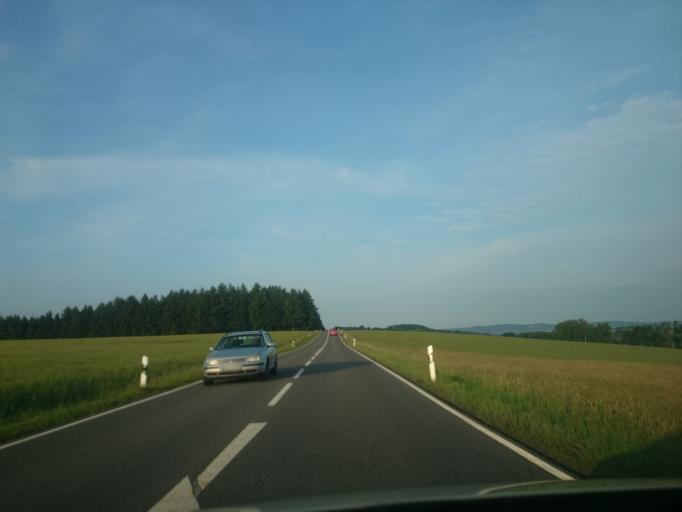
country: DE
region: Saxony
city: Grosshartmannsdorf
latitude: 50.7607
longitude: 13.3080
